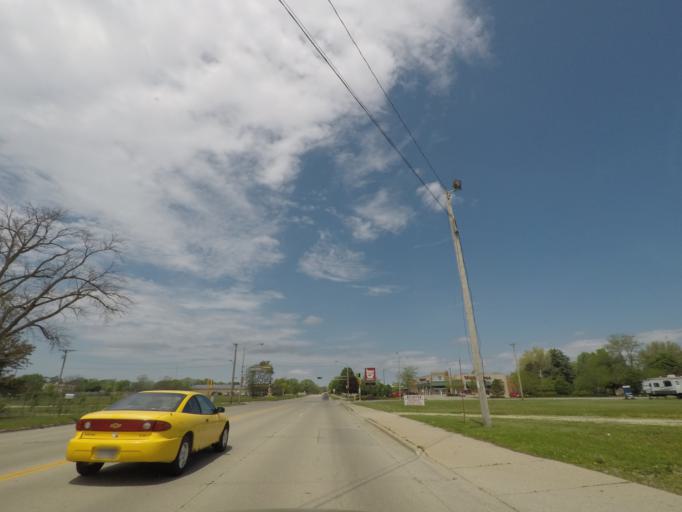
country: US
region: Wisconsin
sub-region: Rock County
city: Beloit
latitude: 42.5181
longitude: -89.0650
